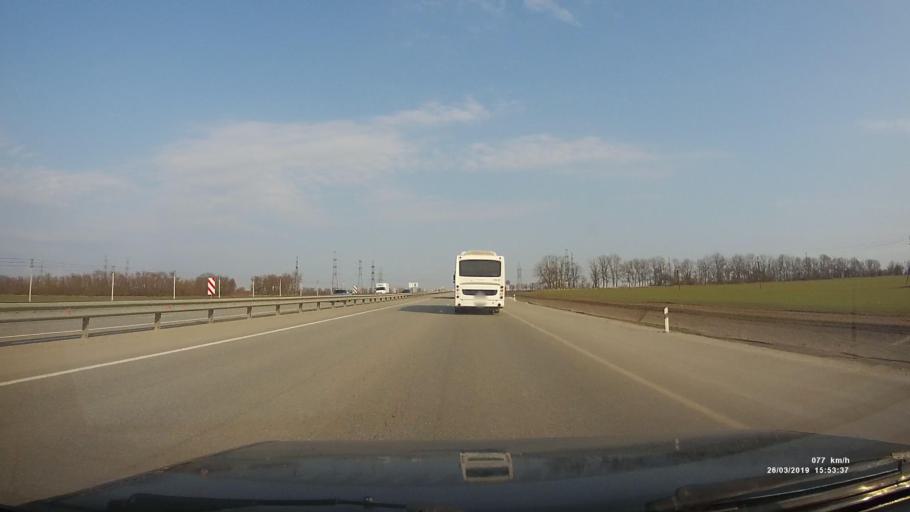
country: RU
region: Rostov
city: Krym
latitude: 47.2722
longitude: 39.5434
